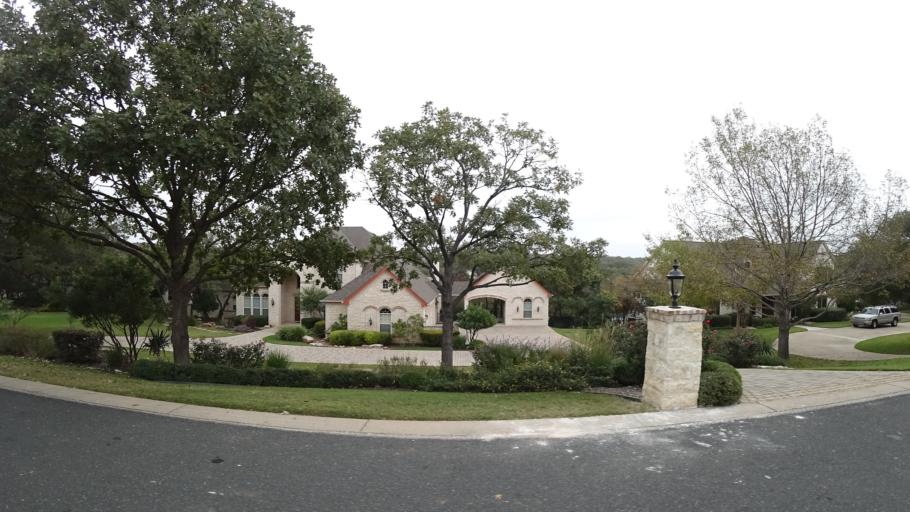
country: US
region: Texas
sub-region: Williamson County
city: Anderson Mill
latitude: 30.4429
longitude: -97.8205
